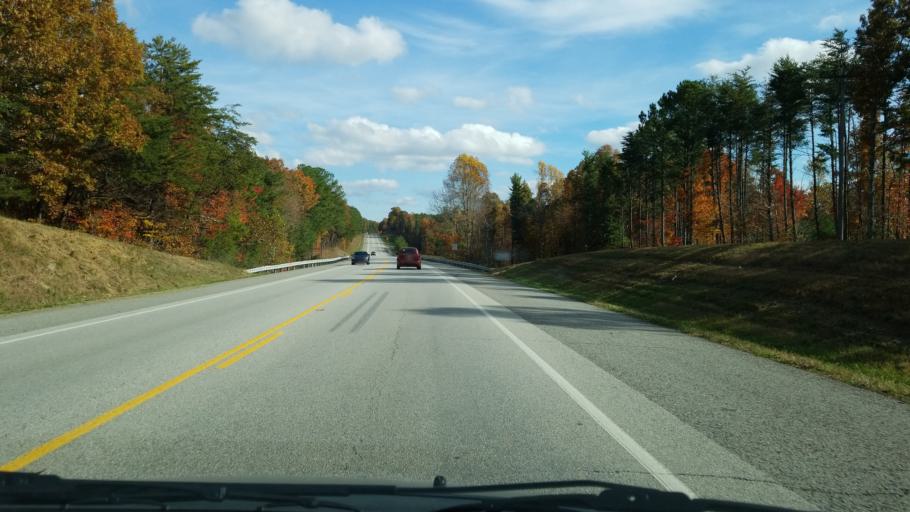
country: US
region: Tennessee
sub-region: Sequatchie County
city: Dunlap
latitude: 35.4429
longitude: -85.4316
